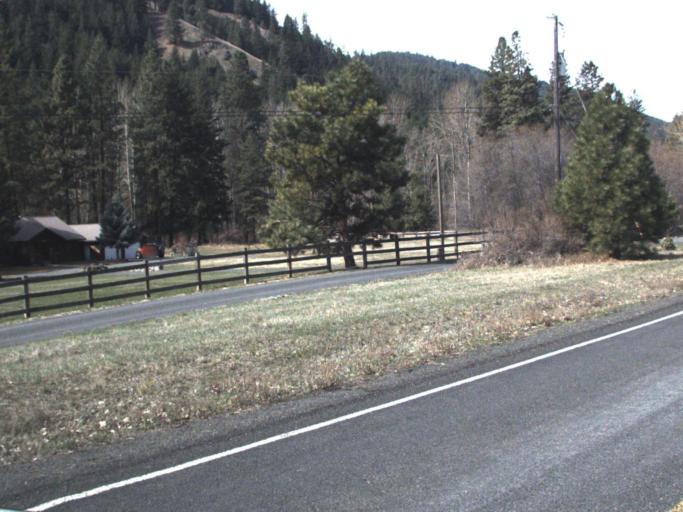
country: US
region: Washington
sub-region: Kittitas County
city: Cle Elum
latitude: 46.8976
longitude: -121.0062
